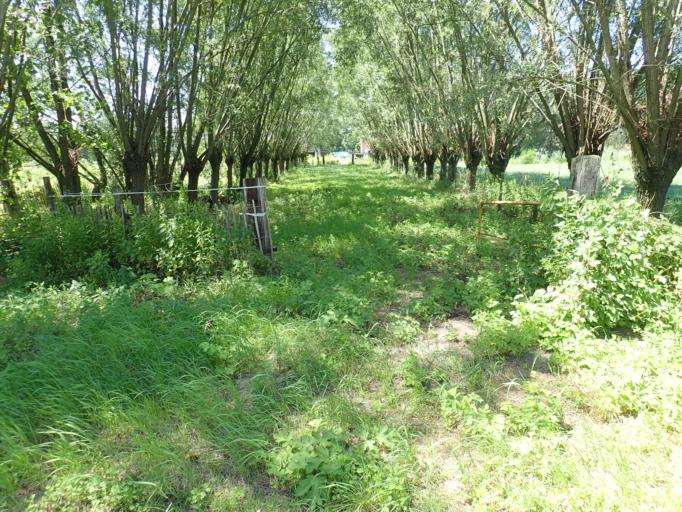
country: BE
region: Flanders
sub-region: Provincie Antwerpen
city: Beerse
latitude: 51.2932
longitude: 4.8362
